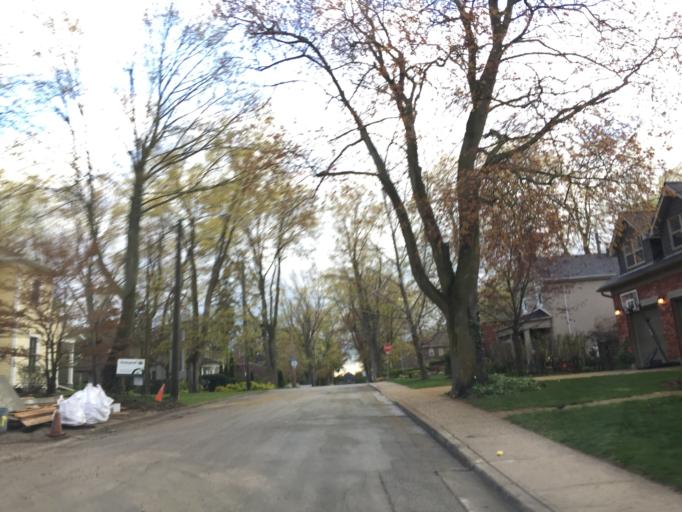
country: CA
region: Ontario
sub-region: Wellington County
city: Guelph
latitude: 43.5538
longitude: -80.2475
